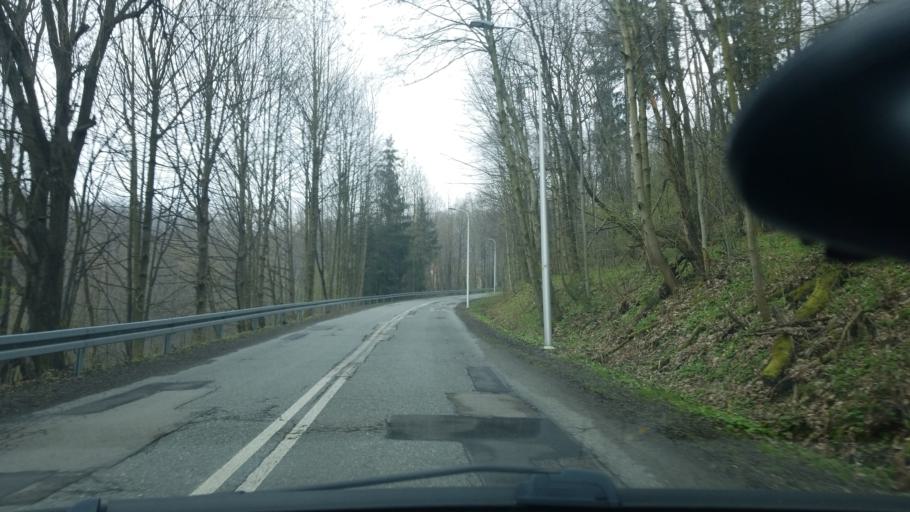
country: PL
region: Silesian Voivodeship
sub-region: Powiat cieszynski
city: Ustron
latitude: 49.7061
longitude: 18.8315
